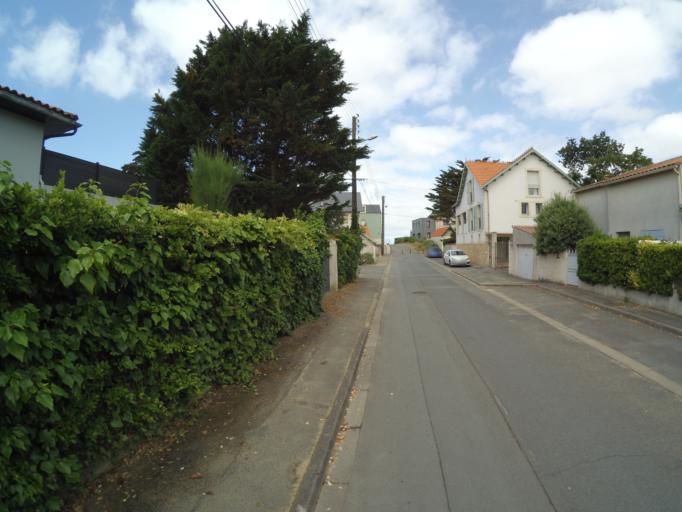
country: FR
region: Poitou-Charentes
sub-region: Departement de la Charente-Maritime
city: Chatelaillon-Plage
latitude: 46.0656
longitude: -1.0918
